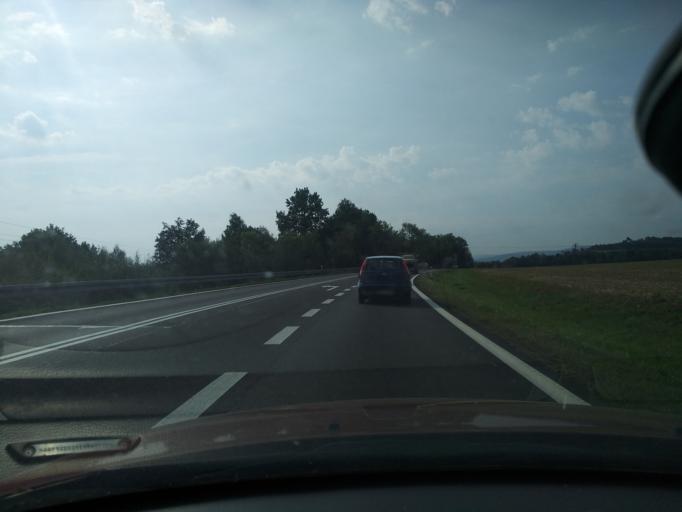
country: PL
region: Lower Silesian Voivodeship
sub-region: Powiat lwowecki
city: Gryfow Slaski
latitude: 51.0220
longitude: 15.4310
